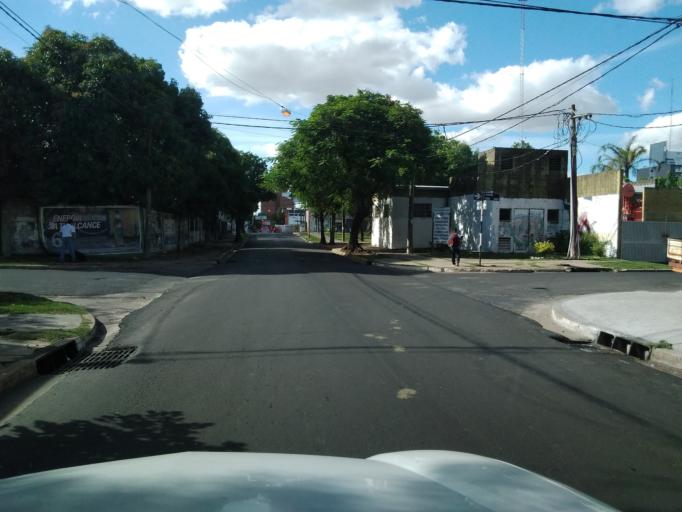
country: AR
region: Corrientes
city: Corrientes
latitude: -27.4773
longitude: -58.8367
